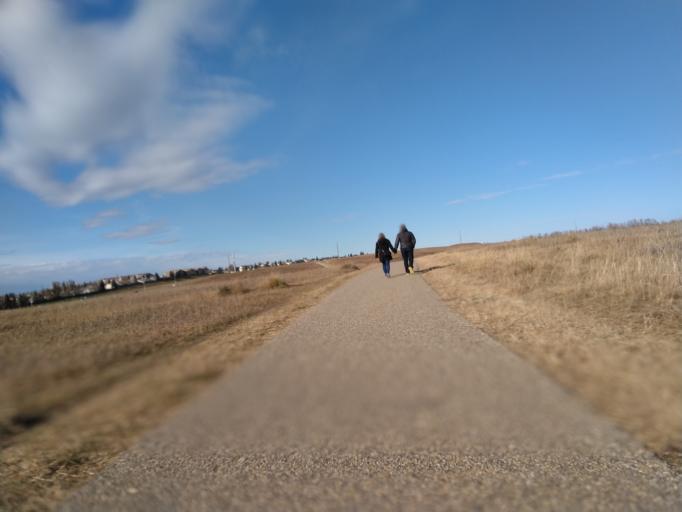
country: CA
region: Alberta
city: Calgary
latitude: 51.1210
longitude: -114.1298
